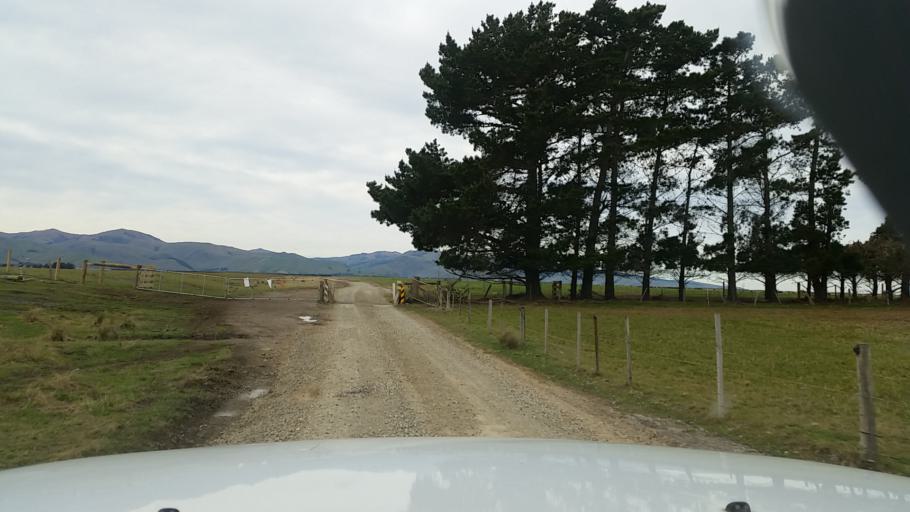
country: NZ
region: Canterbury
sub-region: Selwyn District
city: Lincoln
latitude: -43.8201
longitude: 172.5856
